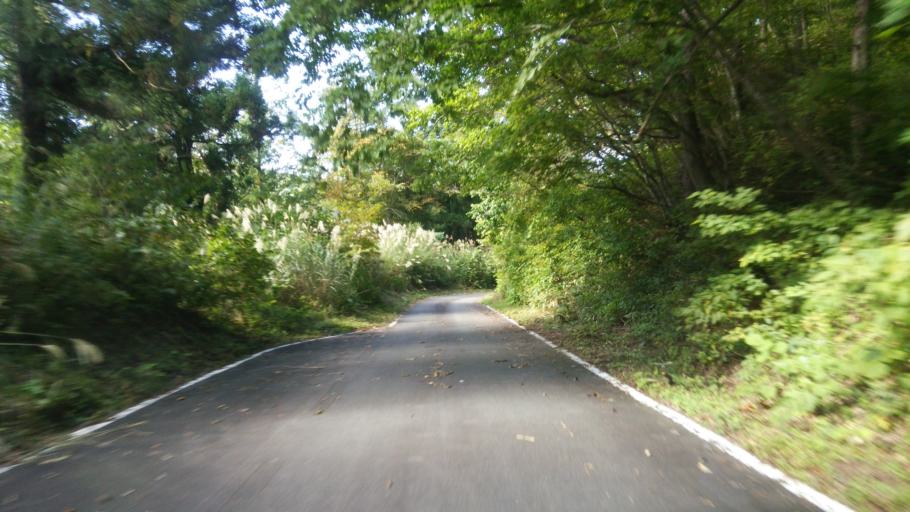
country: JP
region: Fukushima
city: Kitakata
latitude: 37.6142
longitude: 139.9800
